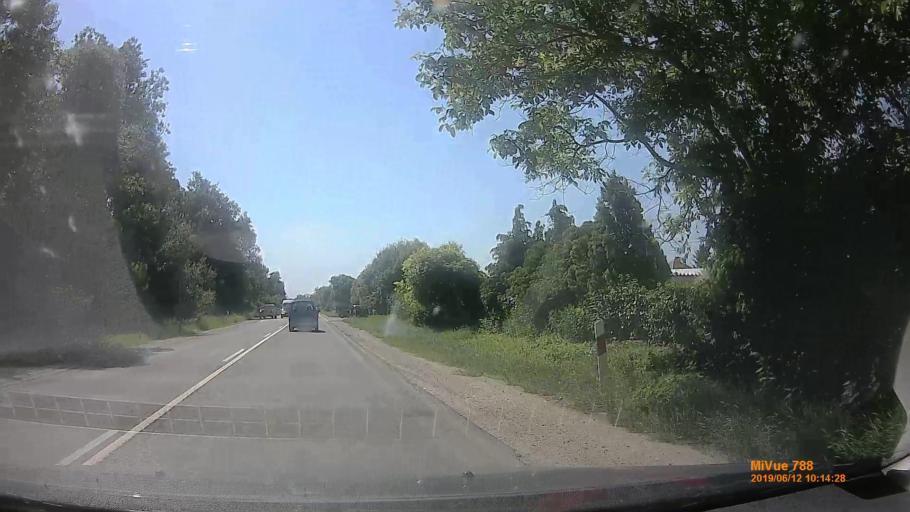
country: HU
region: Pest
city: Dabas
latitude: 47.2118
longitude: 19.2832
